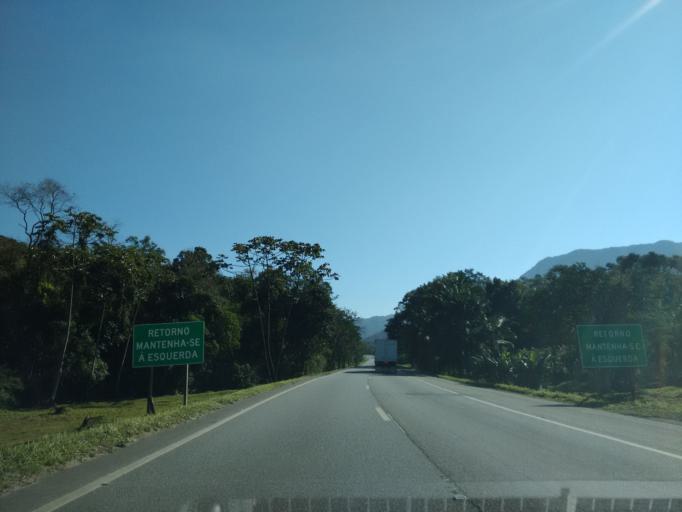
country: BR
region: Parana
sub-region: Guaratuba
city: Guaratuba
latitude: -25.9371
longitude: -48.9089
